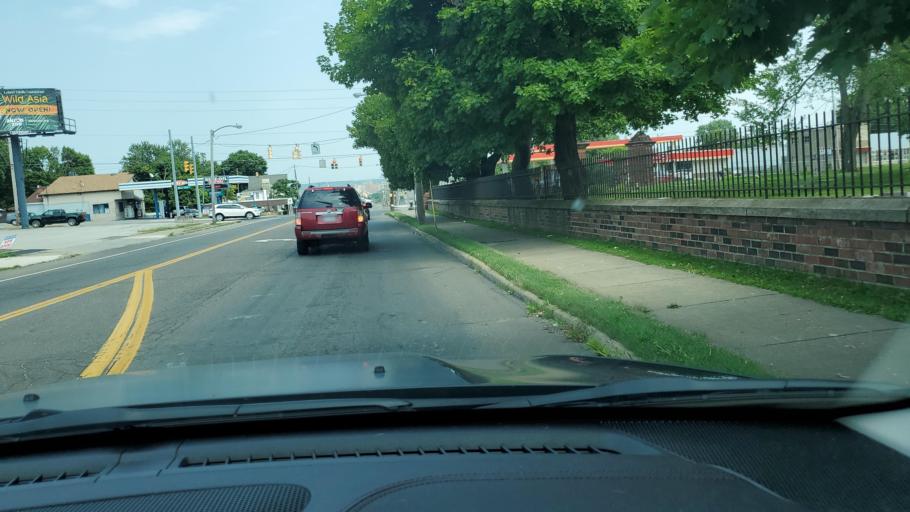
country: US
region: Ohio
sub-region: Mahoning County
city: Youngstown
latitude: 41.1025
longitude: -80.6895
